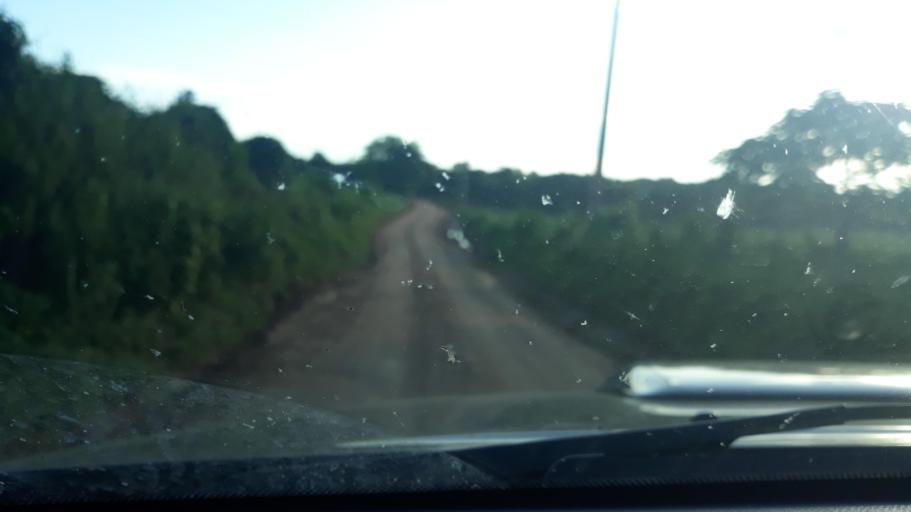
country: BR
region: Bahia
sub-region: Riacho De Santana
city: Riacho de Santana
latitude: -13.8283
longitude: -42.7282
